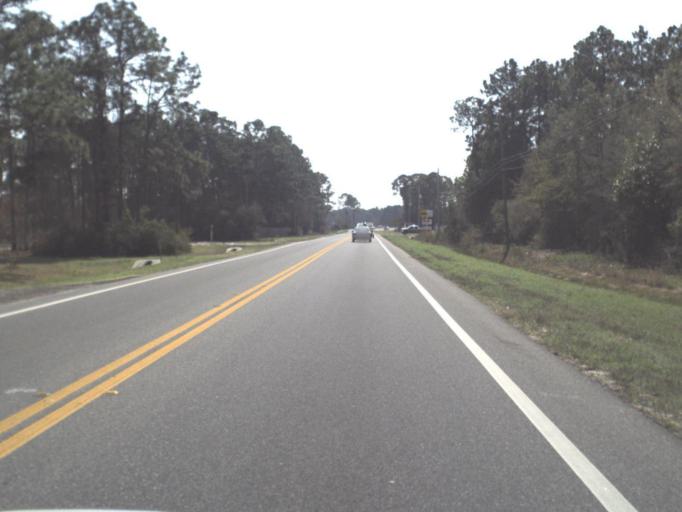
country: US
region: Florida
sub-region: Bay County
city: Pretty Bayou
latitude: 30.2098
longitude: -85.6719
